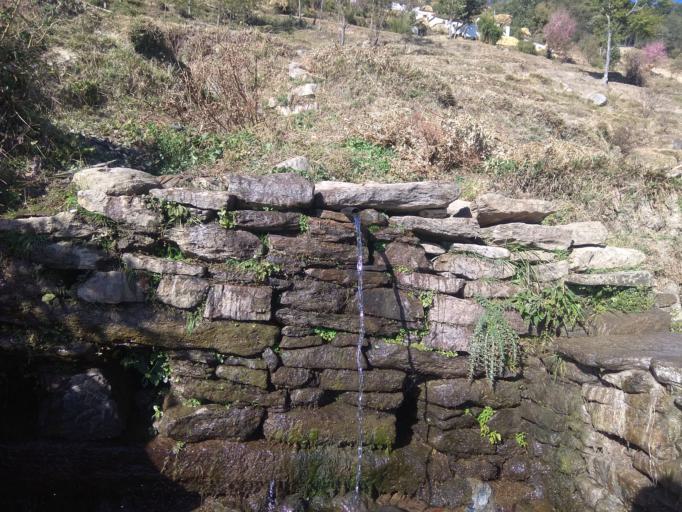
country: NP
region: Far Western
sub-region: Seti Zone
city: Achham
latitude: 29.2562
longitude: 81.6378
